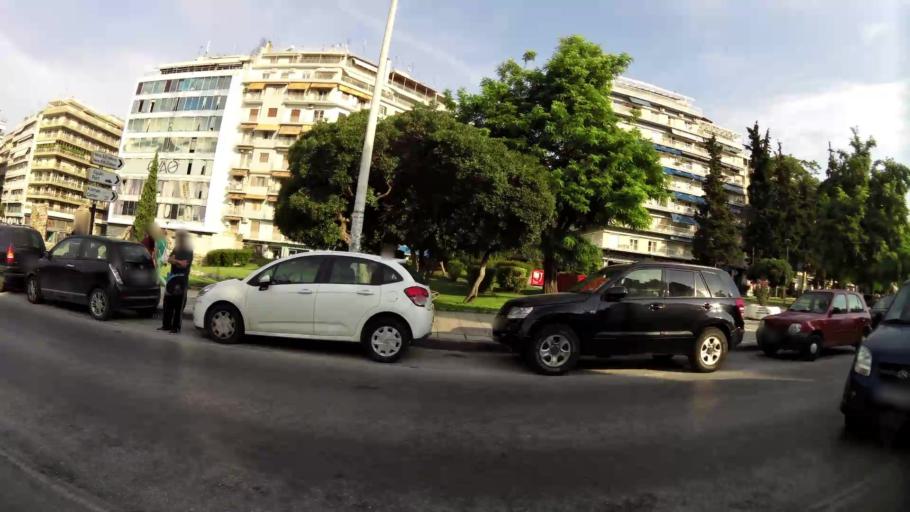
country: GR
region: Central Macedonia
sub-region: Nomos Thessalonikis
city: Agios Pavlos
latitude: 40.6315
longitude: 22.9538
